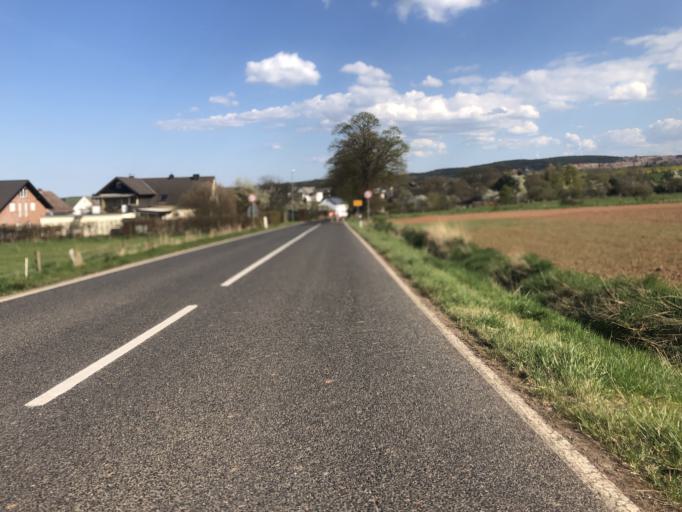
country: DE
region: North Rhine-Westphalia
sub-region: Regierungsbezirk Koln
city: Kall
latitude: 50.5864
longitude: 6.5817
